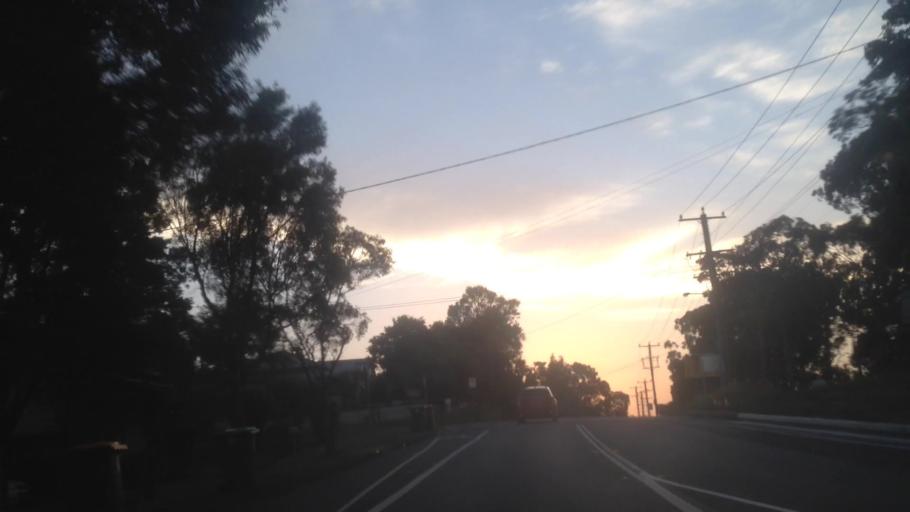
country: AU
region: New South Wales
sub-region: Lake Macquarie Shire
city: Dora Creek
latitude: -33.1069
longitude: 151.4957
